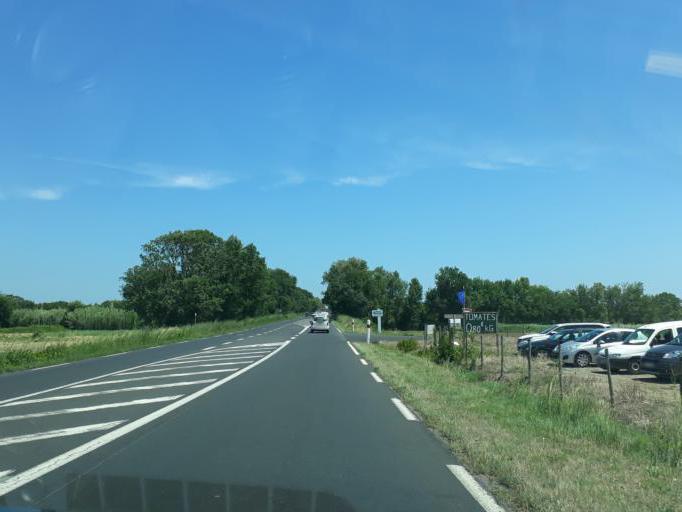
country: FR
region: Languedoc-Roussillon
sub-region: Departement de l'Herault
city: Vias
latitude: 43.3135
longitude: 3.3888
